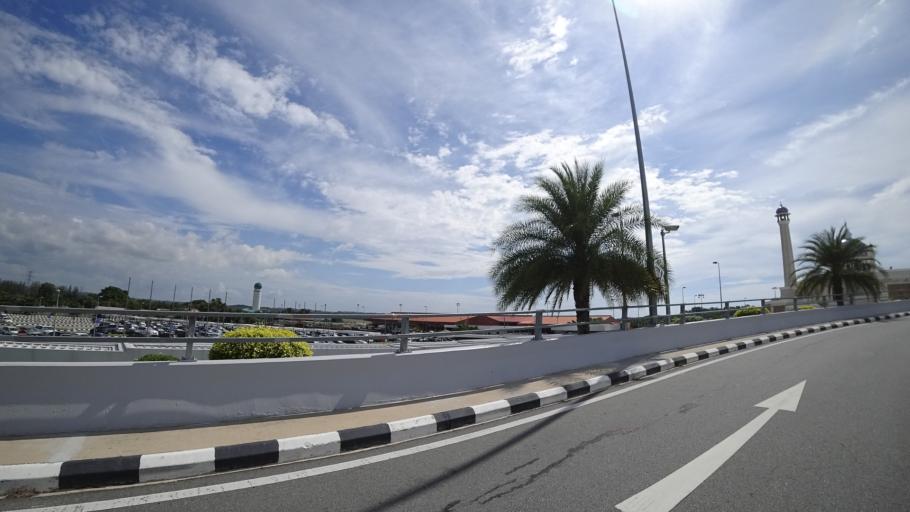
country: BN
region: Brunei and Muara
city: Bandar Seri Begawan
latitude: 4.9432
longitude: 114.9345
